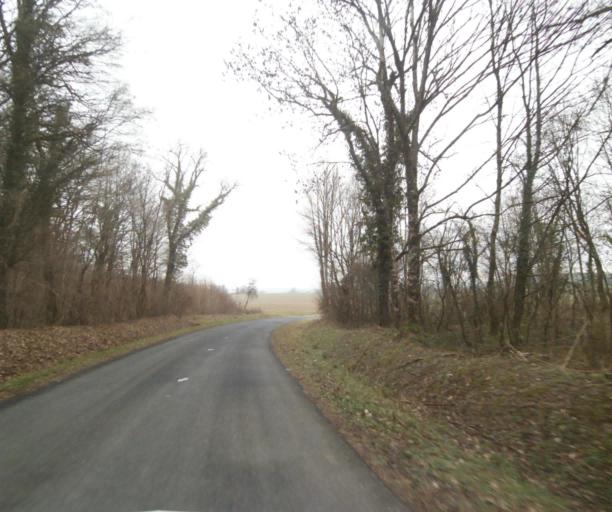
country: FR
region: Champagne-Ardenne
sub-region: Departement de la Haute-Marne
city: Bienville
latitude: 48.5711
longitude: 5.0202
